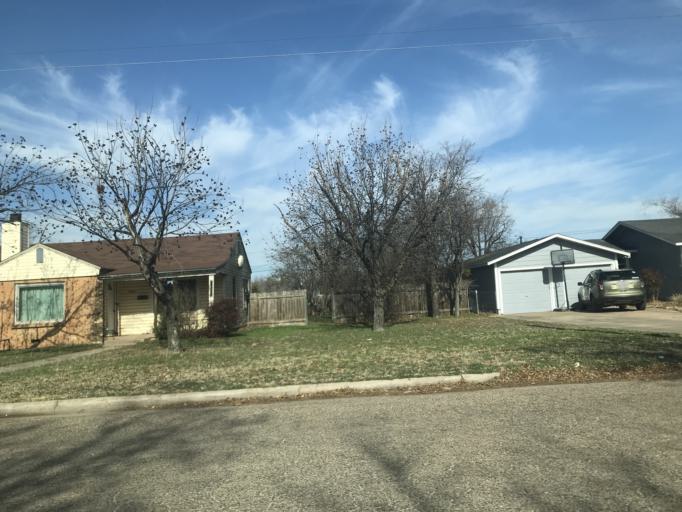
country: US
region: Texas
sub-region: Taylor County
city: Abilene
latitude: 32.4211
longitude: -99.7537
